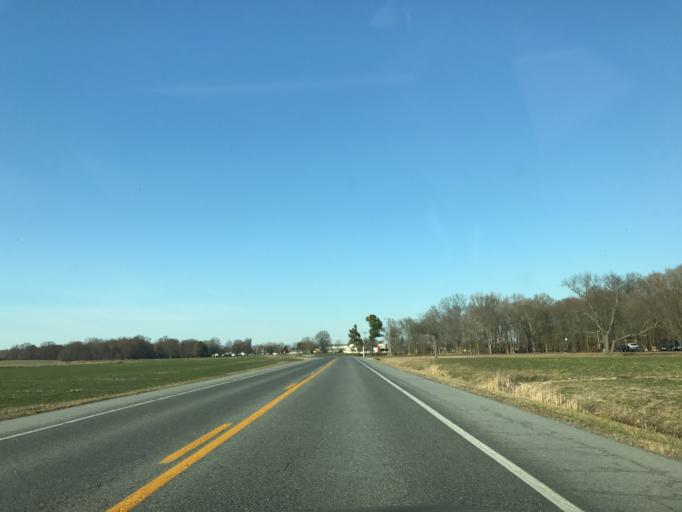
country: US
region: Maryland
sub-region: Caroline County
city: Greensboro
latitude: 39.1336
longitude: -75.8646
